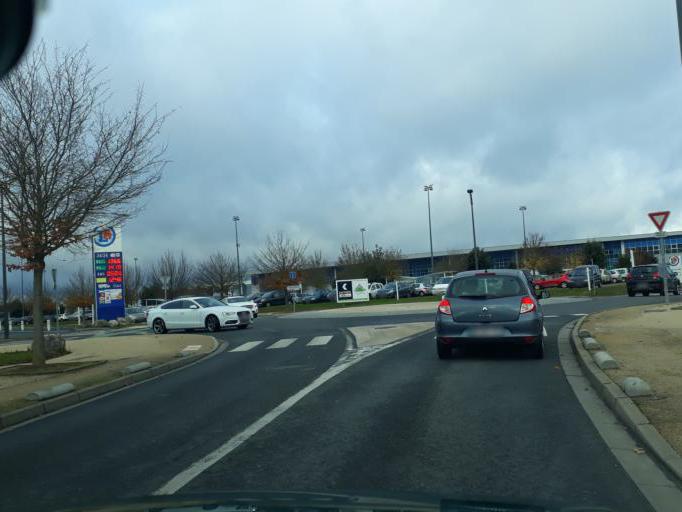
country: FR
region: Centre
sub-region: Departement du Loir-et-Cher
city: Villebarou
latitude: 47.6138
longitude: 1.3265
